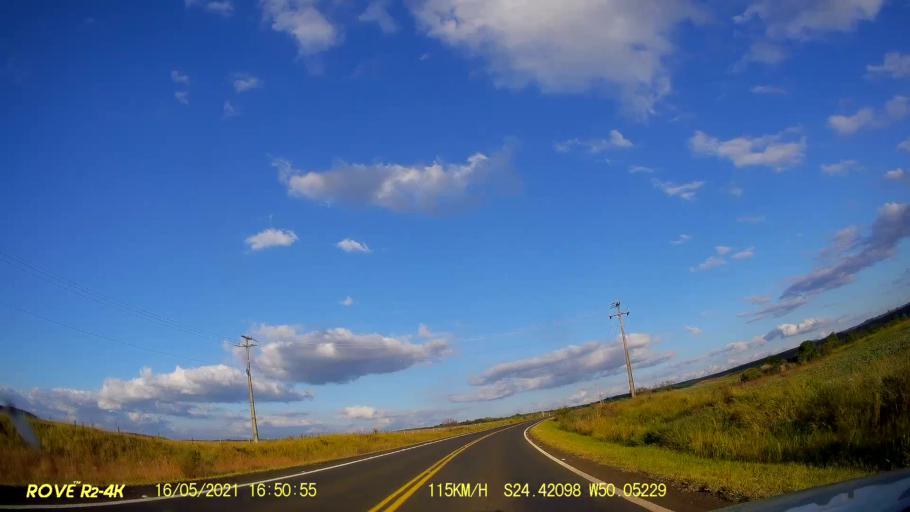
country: BR
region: Parana
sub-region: Pirai Do Sul
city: Pirai do Sul
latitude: -24.4210
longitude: -50.0522
